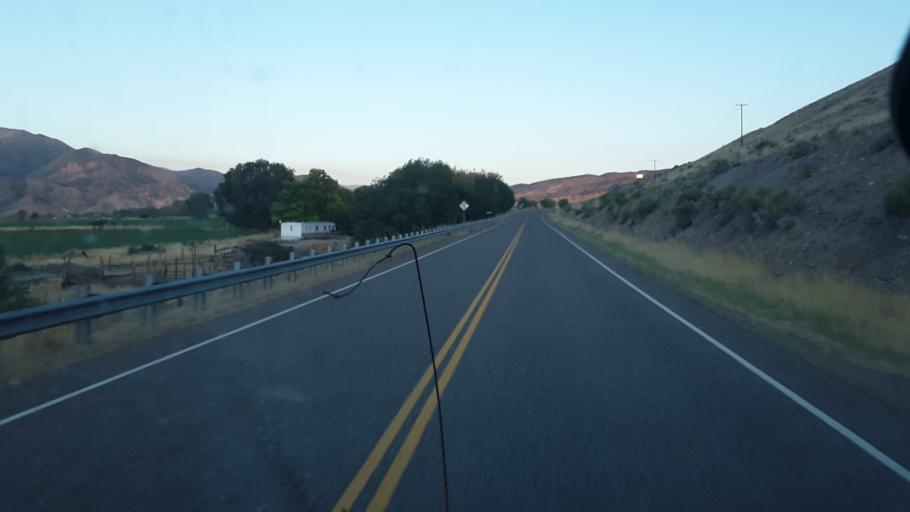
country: US
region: Utah
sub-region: Sevier County
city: Monroe
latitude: 38.6038
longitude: -112.2333
